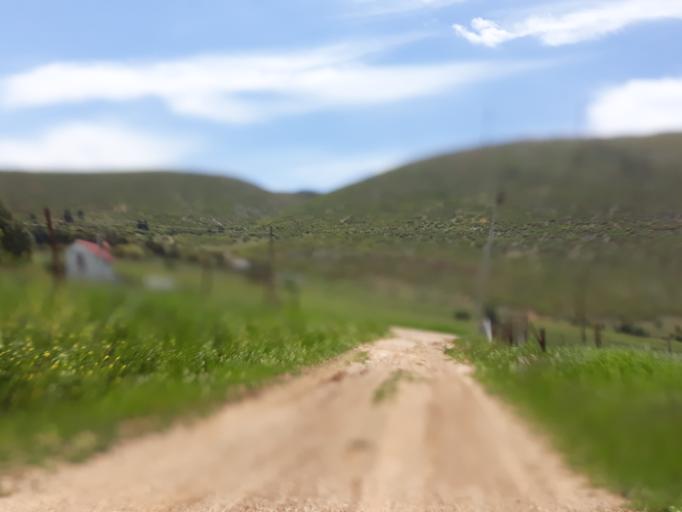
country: GR
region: Central Greece
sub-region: Nomos Voiotias
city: Ayios Thomas
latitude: 38.1827
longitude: 23.5621
